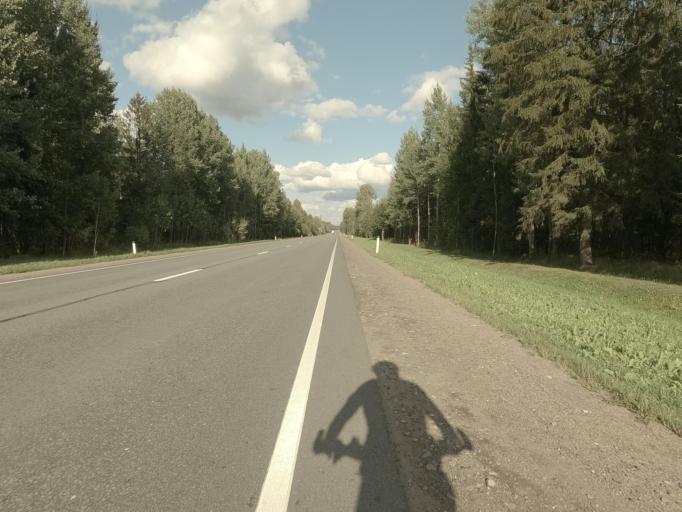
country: RU
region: Leningrad
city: Nikol'skoye
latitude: 59.6727
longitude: 30.9120
